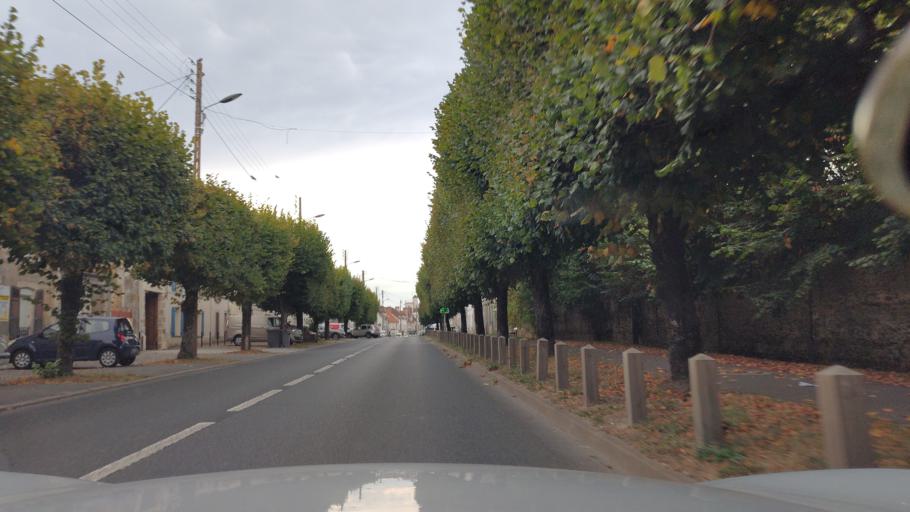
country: FR
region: Ile-de-France
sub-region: Departement de Seine-et-Marne
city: Guignes
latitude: 48.6344
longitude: 2.8022
